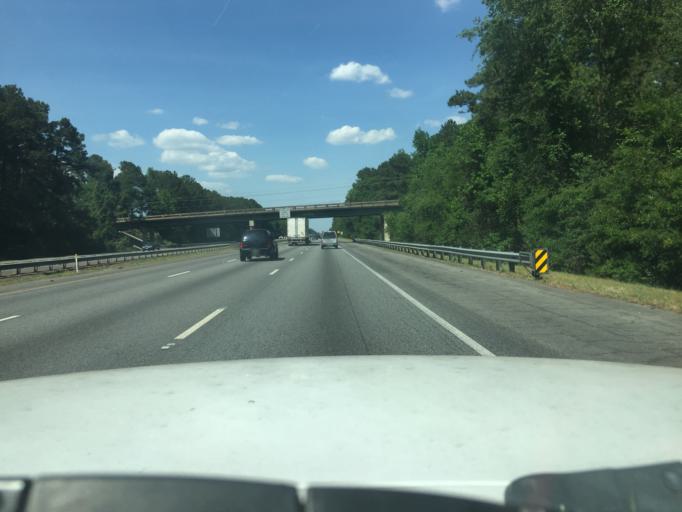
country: US
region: Georgia
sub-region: Chatham County
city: Georgetown
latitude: 32.0266
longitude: -81.2698
